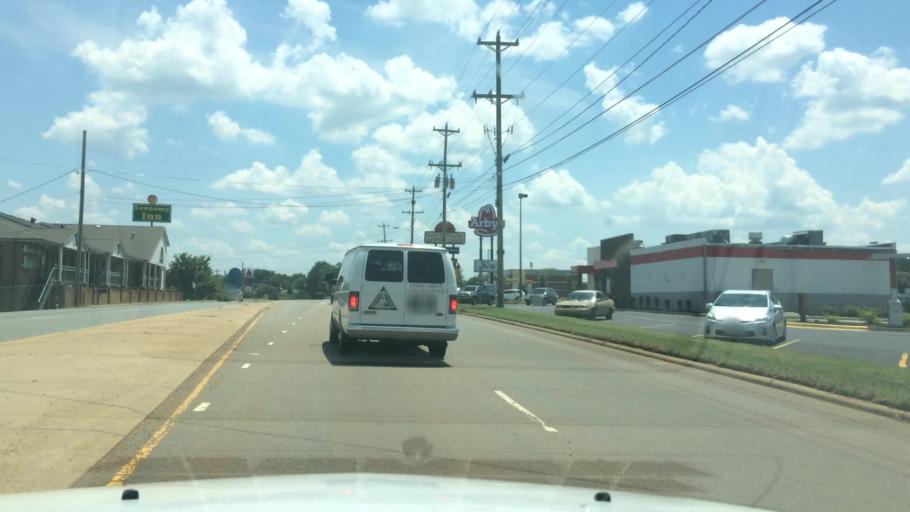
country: US
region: North Carolina
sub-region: Iredell County
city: Statesville
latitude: 35.7975
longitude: -80.9392
